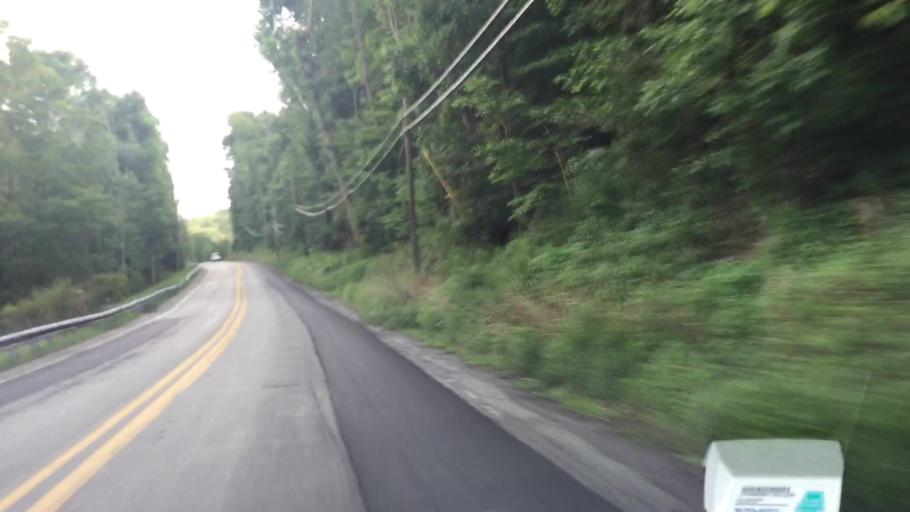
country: US
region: Pennsylvania
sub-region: Allegheny County
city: West View
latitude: 40.5552
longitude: -80.0579
